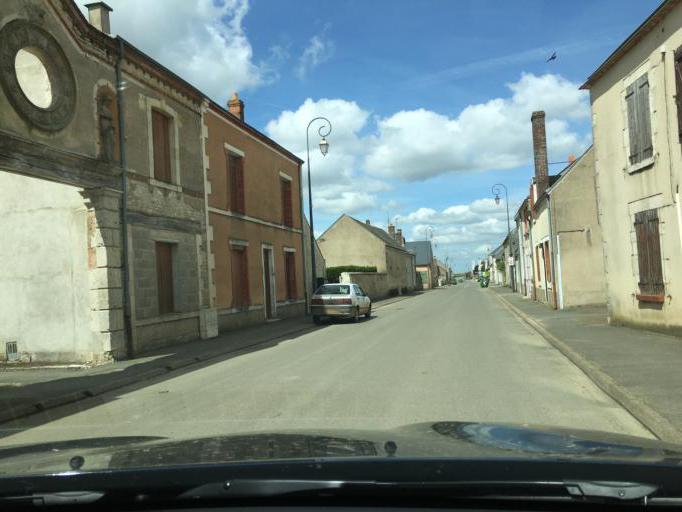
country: FR
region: Centre
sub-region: Departement du Loiret
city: Patay
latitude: 48.0826
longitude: 1.7405
